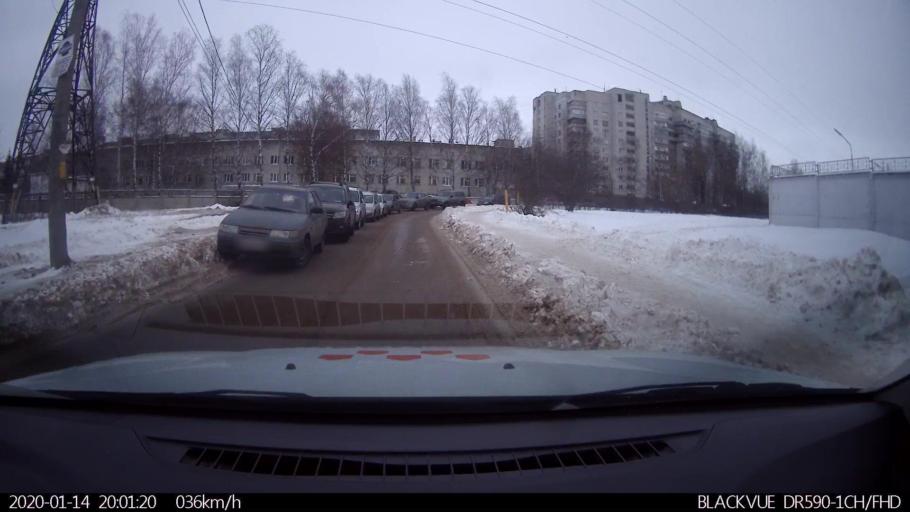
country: RU
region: Nizjnij Novgorod
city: Nizhniy Novgorod
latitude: 56.2340
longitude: 43.9431
